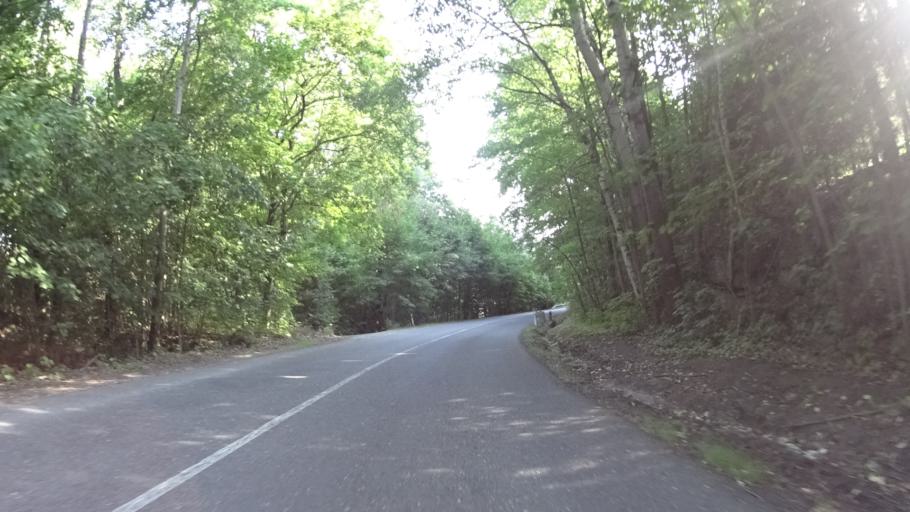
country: CZ
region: Liberecky
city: Hodkovice nad Mohelkou
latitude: 50.6503
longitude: 15.1062
